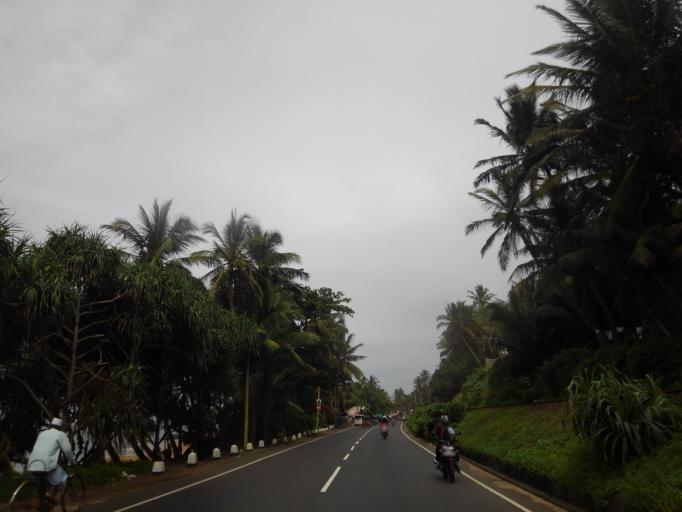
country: LK
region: Western
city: Beruwala
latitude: 6.4929
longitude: 79.9819
